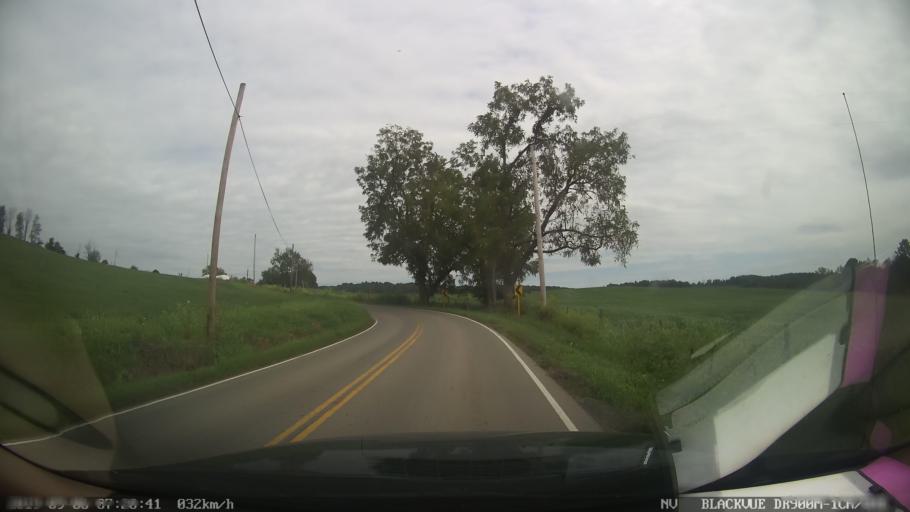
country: US
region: Ohio
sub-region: Licking County
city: Newark
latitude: 40.1294
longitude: -82.3789
